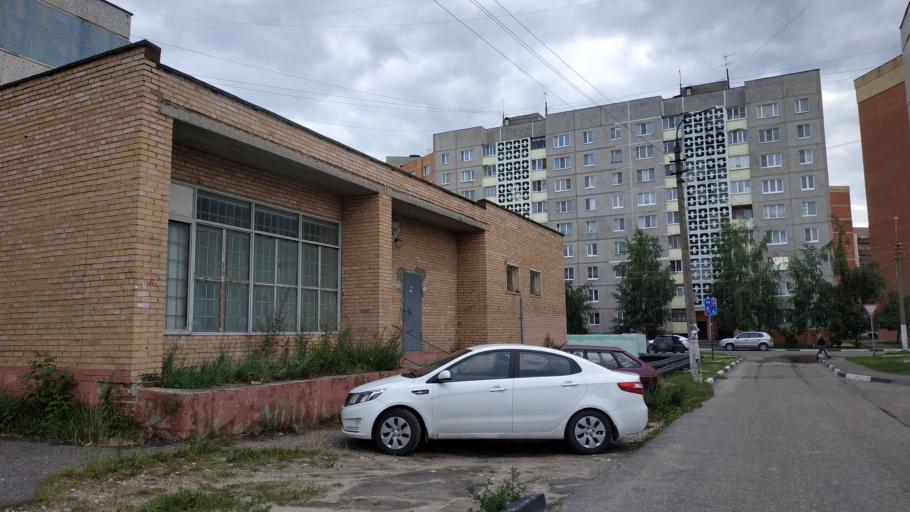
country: RU
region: Moskovskaya
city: Shatura
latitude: 55.5792
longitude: 39.5165
